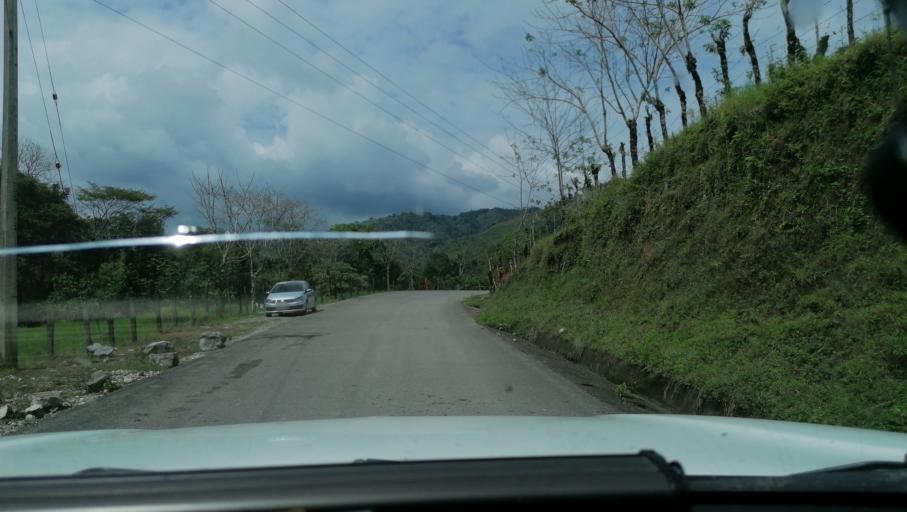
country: MX
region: Chiapas
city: Ocotepec
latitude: 17.3164
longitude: -93.1695
